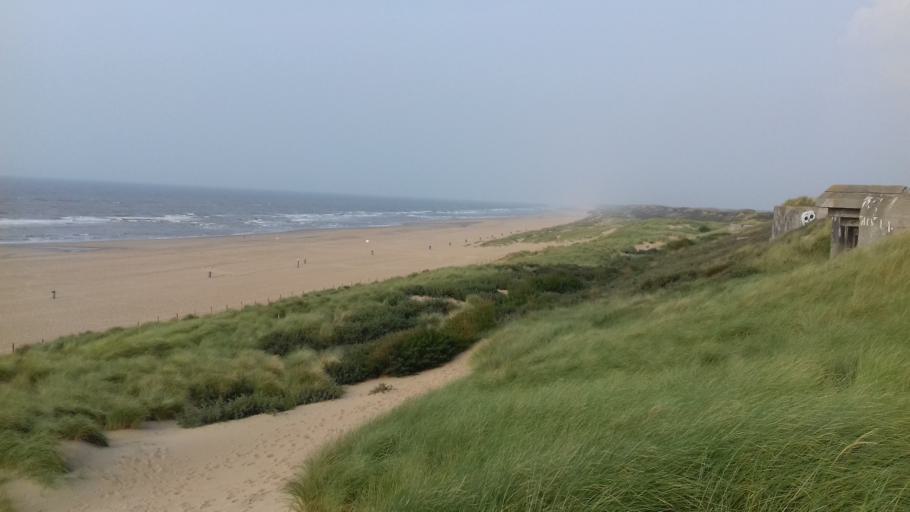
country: NL
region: South Holland
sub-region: Gemeente Den Haag
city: Scheveningen
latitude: 52.1258
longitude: 4.3013
